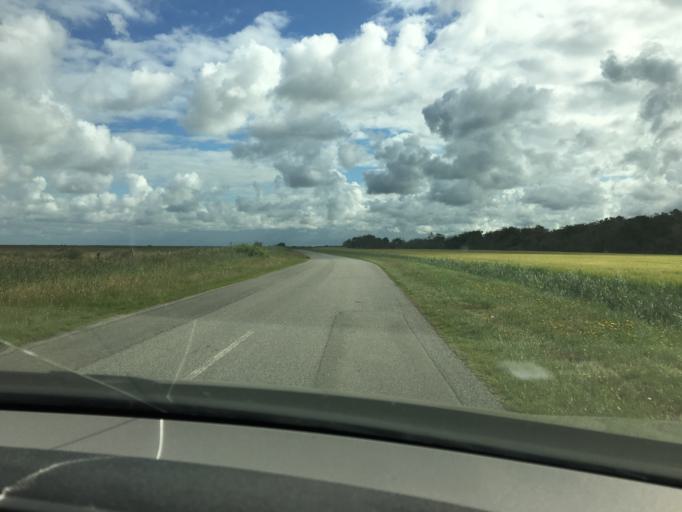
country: DK
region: South Denmark
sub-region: Varde Kommune
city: Oksbol
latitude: 55.8331
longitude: 8.2557
